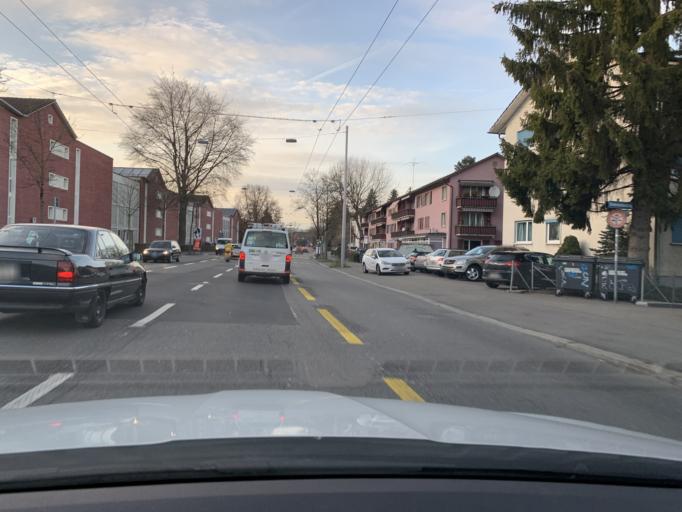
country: CH
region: Zurich
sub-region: Bezirk Zuerich
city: Zuerich (Kreis 11) / Affoltern
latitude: 47.4168
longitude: 8.5108
